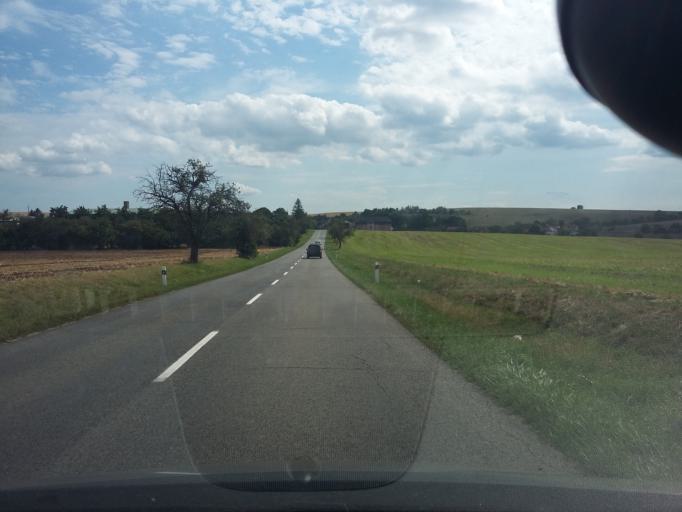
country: SK
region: Trnavsky
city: Gbely
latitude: 48.7300
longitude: 17.1636
